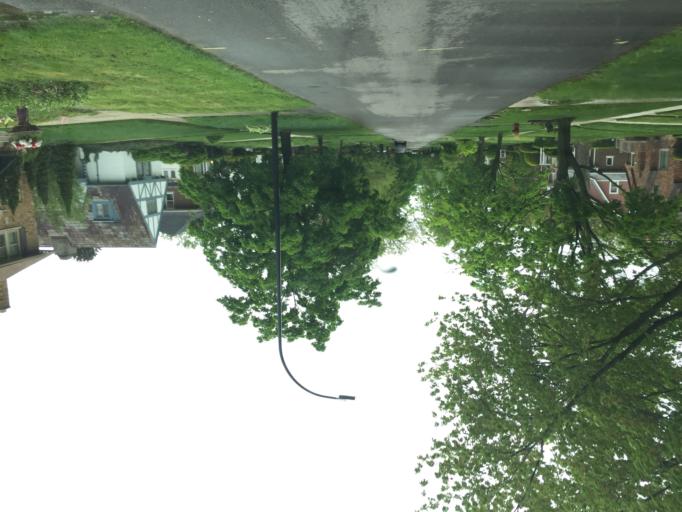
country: US
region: Michigan
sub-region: Oakland County
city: Southfield
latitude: 42.4130
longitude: -83.2304
